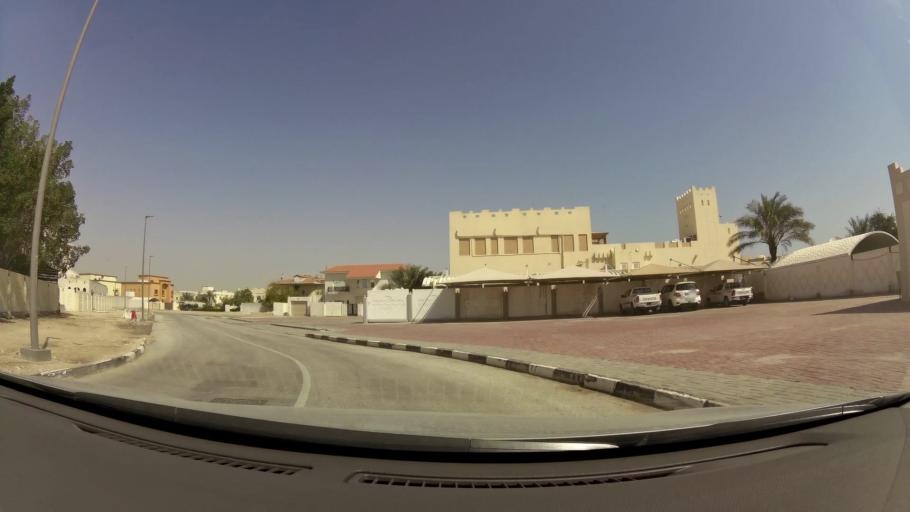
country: QA
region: Baladiyat ad Dawhah
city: Doha
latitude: 25.3635
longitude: 51.5024
